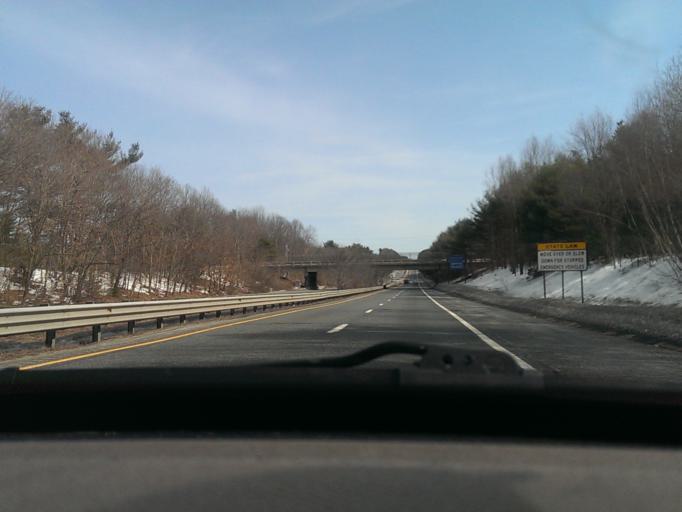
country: US
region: Massachusetts
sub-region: Worcester County
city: Millville
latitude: 42.0130
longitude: -71.5852
